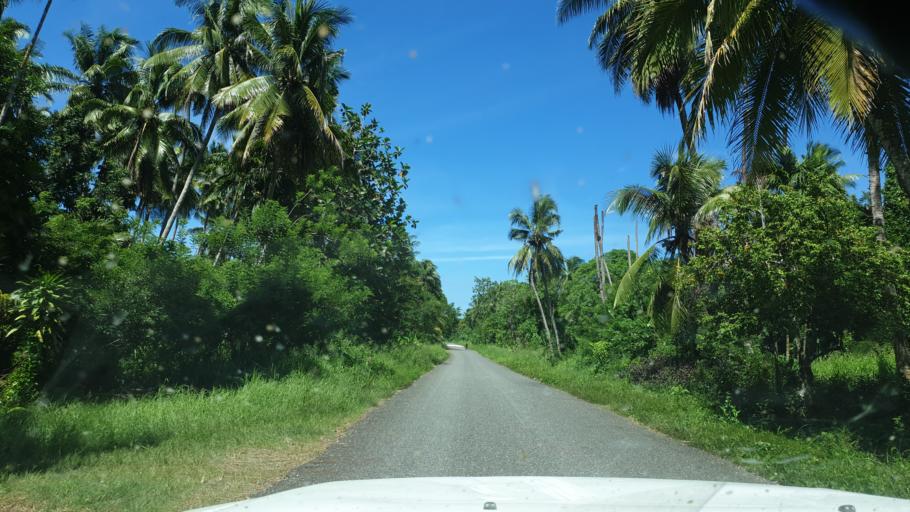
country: PG
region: Madang
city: Madang
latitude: -4.4997
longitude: 145.4243
